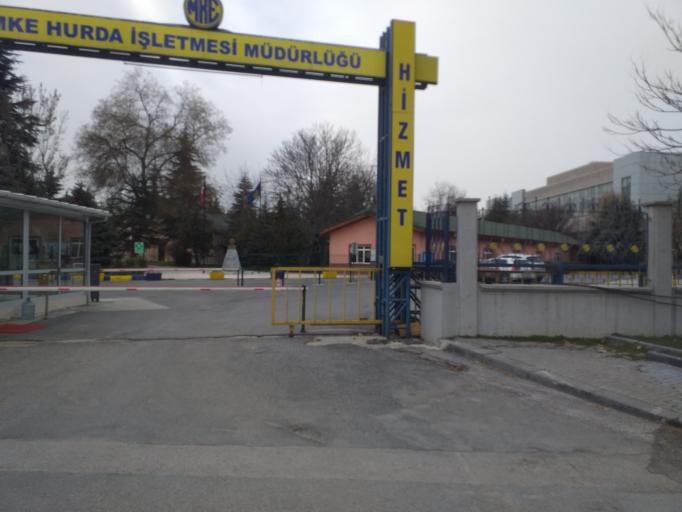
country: TR
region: Ankara
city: Ankara
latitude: 39.9469
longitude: 32.8291
